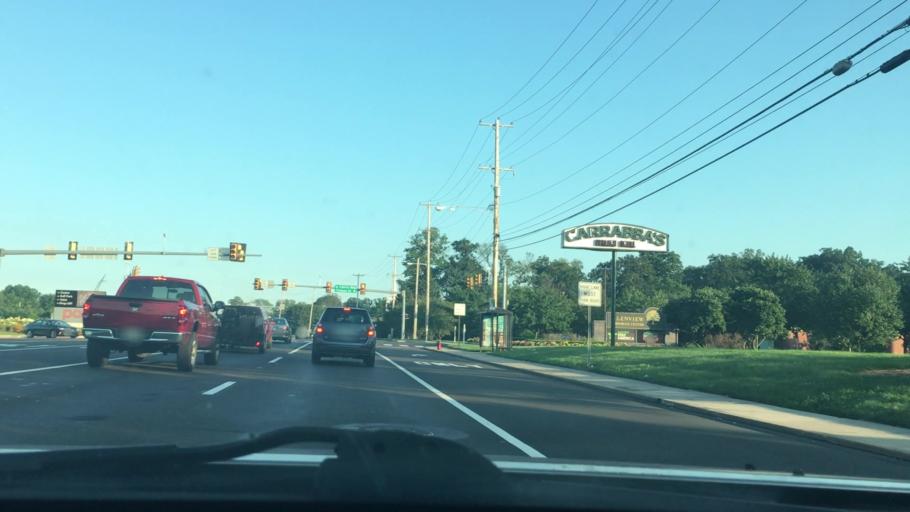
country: US
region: Pennsylvania
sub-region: Bucks County
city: Trevose
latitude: 40.1160
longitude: -74.9585
